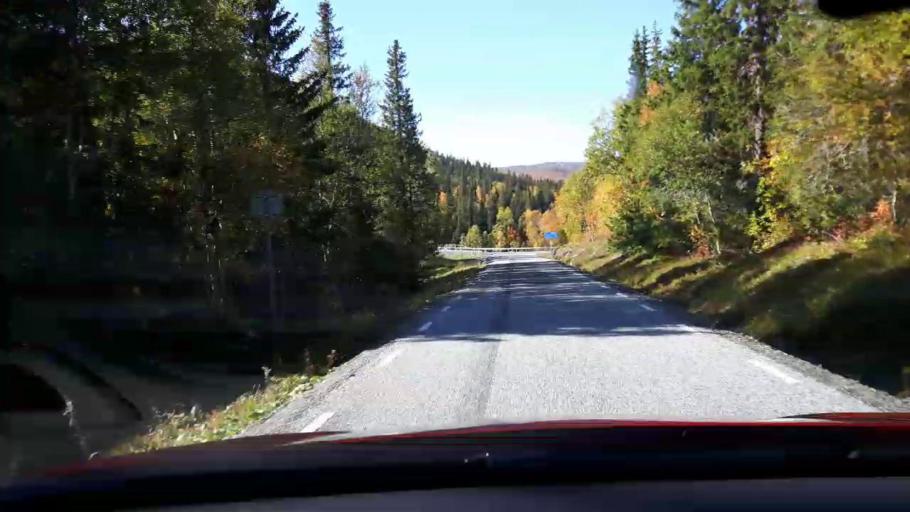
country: NO
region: Nord-Trondelag
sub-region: Royrvik
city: Royrvik
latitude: 64.8778
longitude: 14.2170
